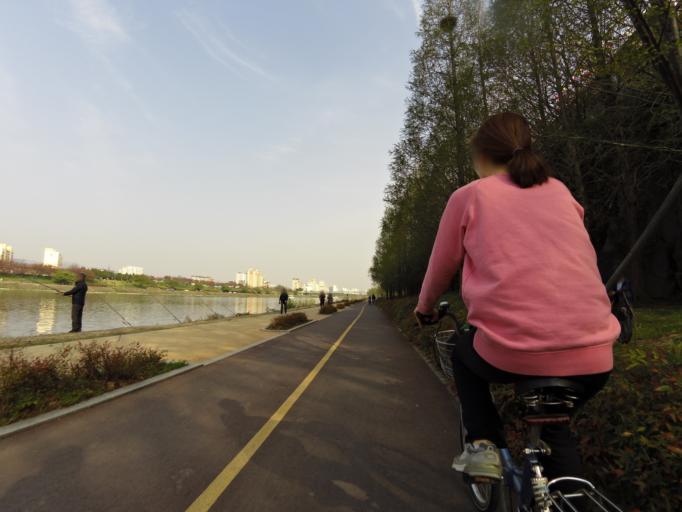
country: KR
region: Daegu
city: Daegu
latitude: 35.8877
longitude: 128.6418
